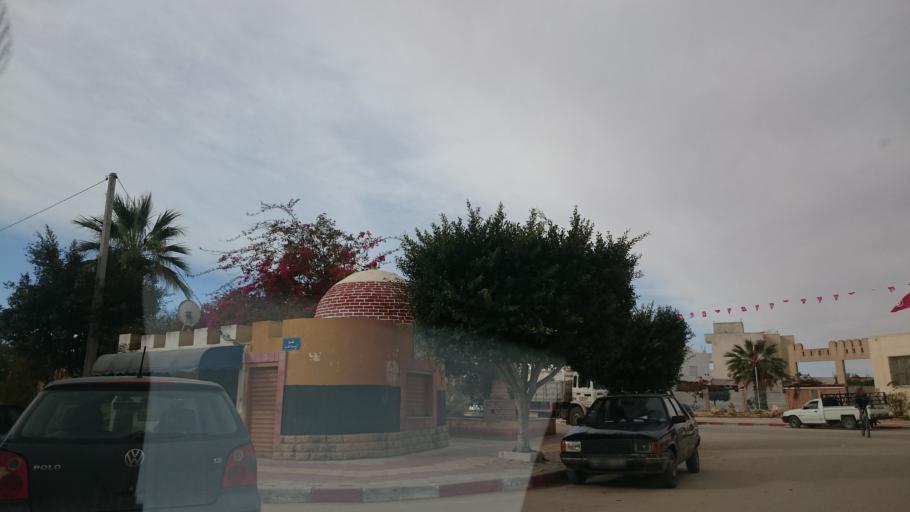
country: TN
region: Safaqis
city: Sfax
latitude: 34.7403
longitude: 10.5291
